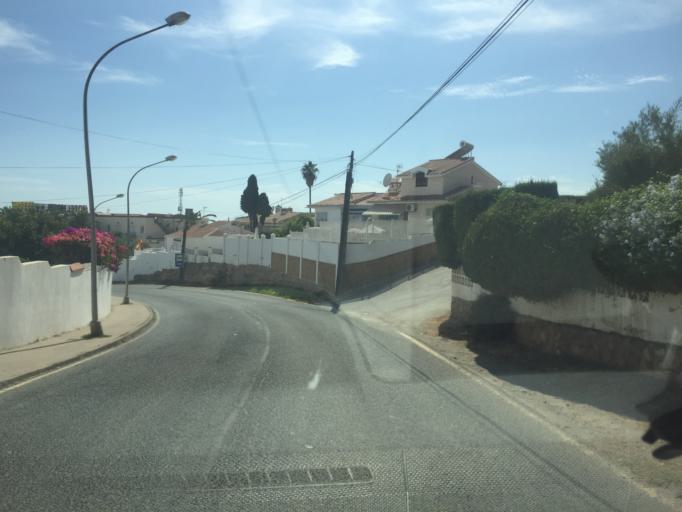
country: ES
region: Andalusia
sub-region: Provincia de Malaga
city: Nerja
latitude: 36.7615
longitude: -3.8477
